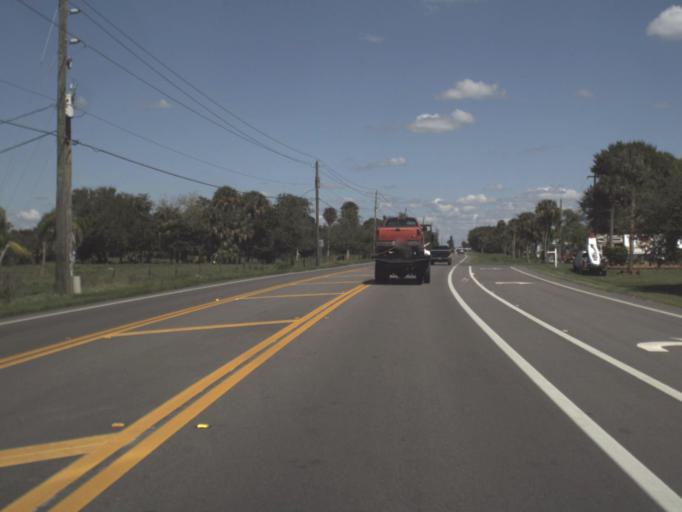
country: US
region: Florida
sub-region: Glades County
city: Buckhead Ridge
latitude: 27.1682
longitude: -80.8593
